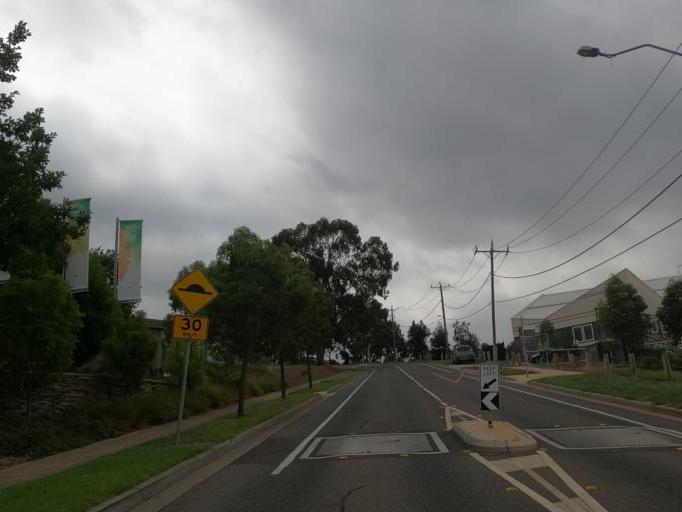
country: AU
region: Victoria
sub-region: Hume
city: Broadmeadows
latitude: -37.6747
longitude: 144.9096
